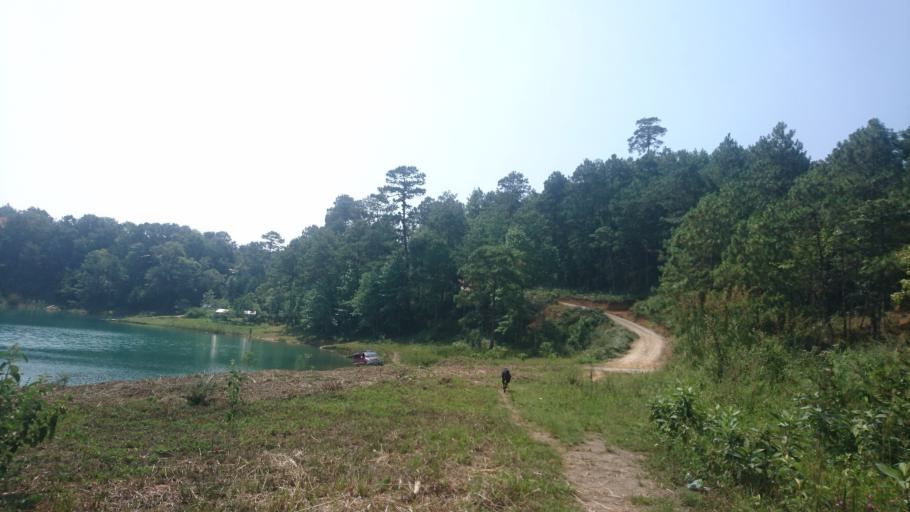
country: GT
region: Huehuetenango
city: Union
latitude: 16.0733
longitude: -91.6826
